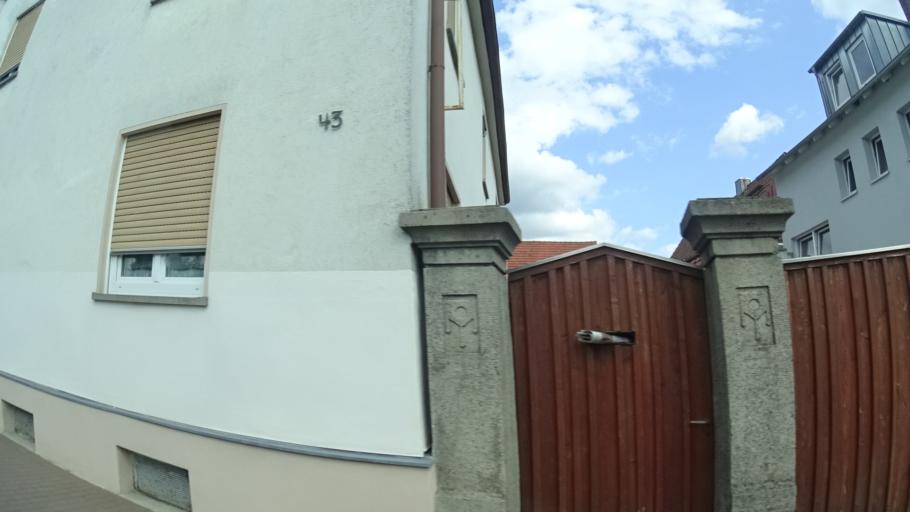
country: DE
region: Bavaria
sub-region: Regierungsbezirk Unterfranken
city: Grafenrheinfeld
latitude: 49.9985
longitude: 10.1979
